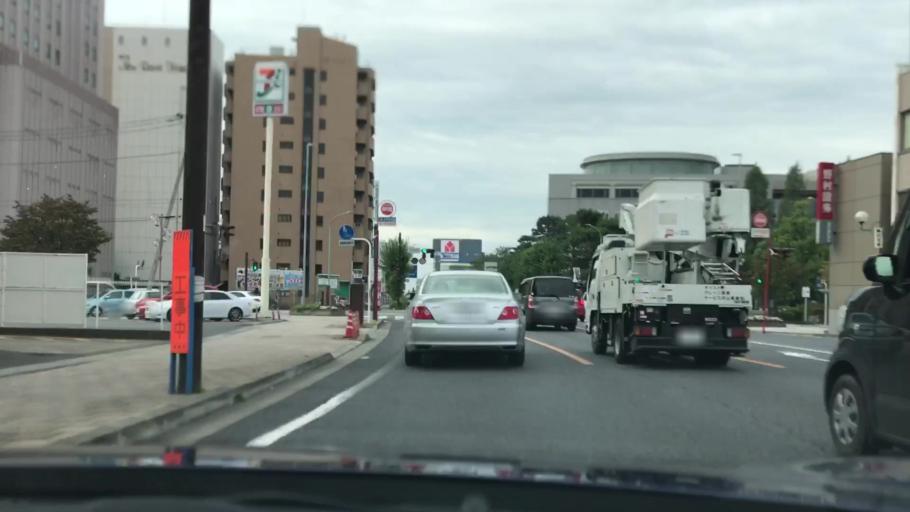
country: JP
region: Gunma
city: Ota
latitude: 36.2924
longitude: 139.3765
